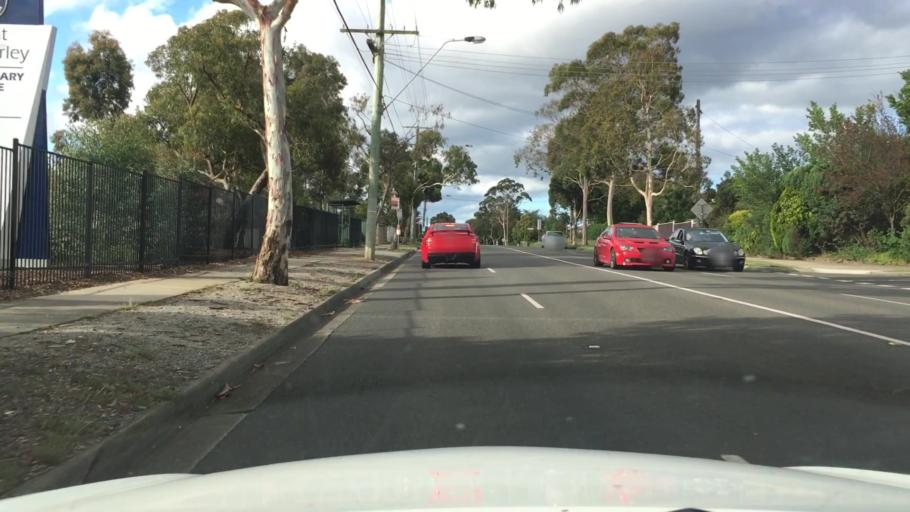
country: AU
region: Victoria
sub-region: Whitehorse
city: Burwood
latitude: -37.8652
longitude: 145.1309
